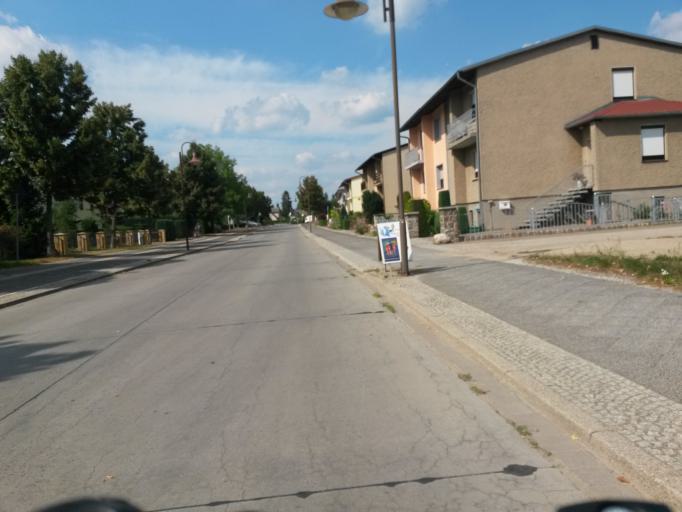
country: DE
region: Brandenburg
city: Templin
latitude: 53.1083
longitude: 13.5190
